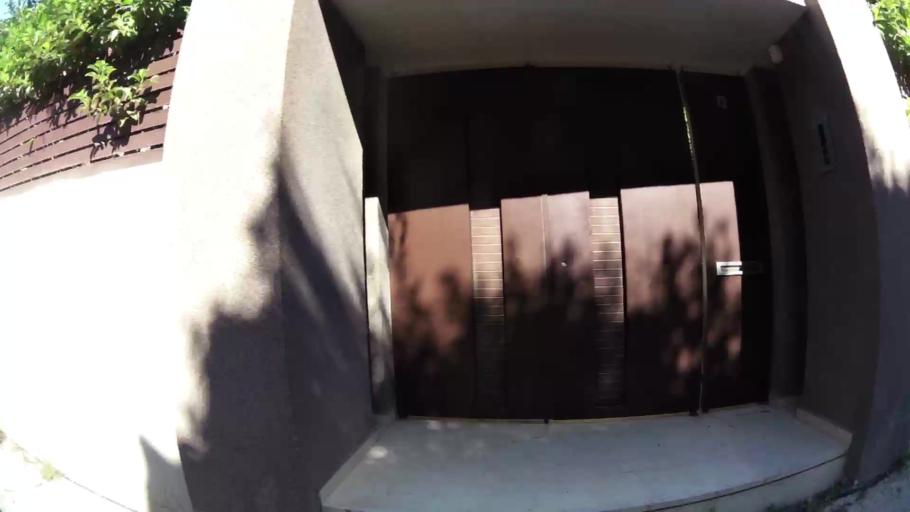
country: GR
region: Attica
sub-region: Nomarchia Athinas
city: Kifisia
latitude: 38.0815
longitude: 23.7998
